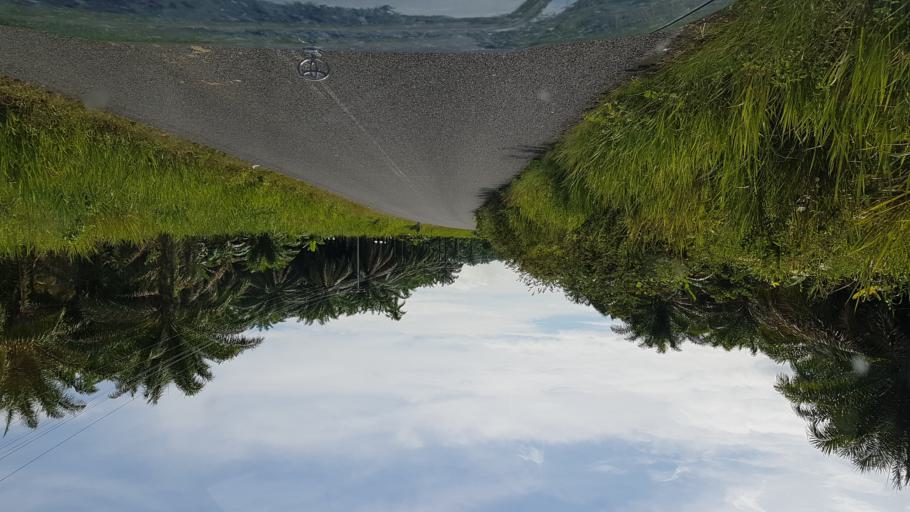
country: PG
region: Northern Province
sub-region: Sohe
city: Popondetta
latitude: -8.7692
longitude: 148.2236
